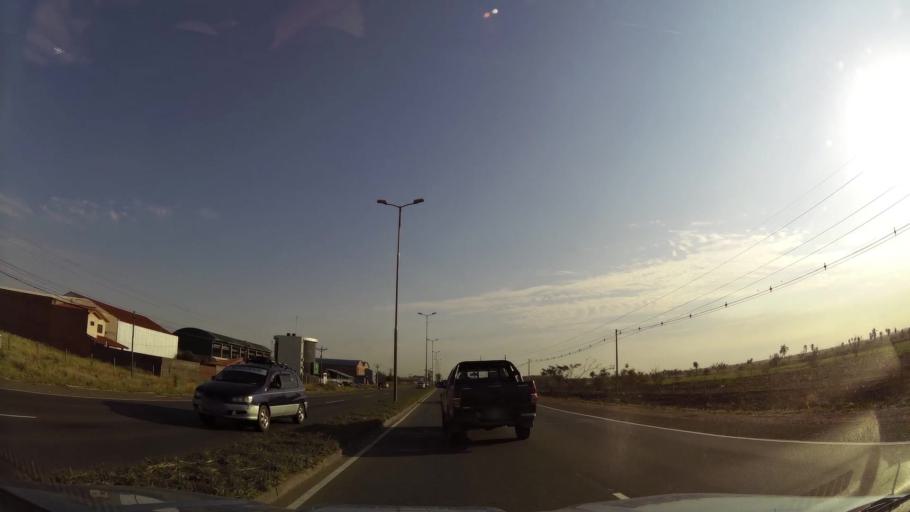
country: BO
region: Santa Cruz
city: La Belgica
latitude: -17.6391
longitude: -63.1577
